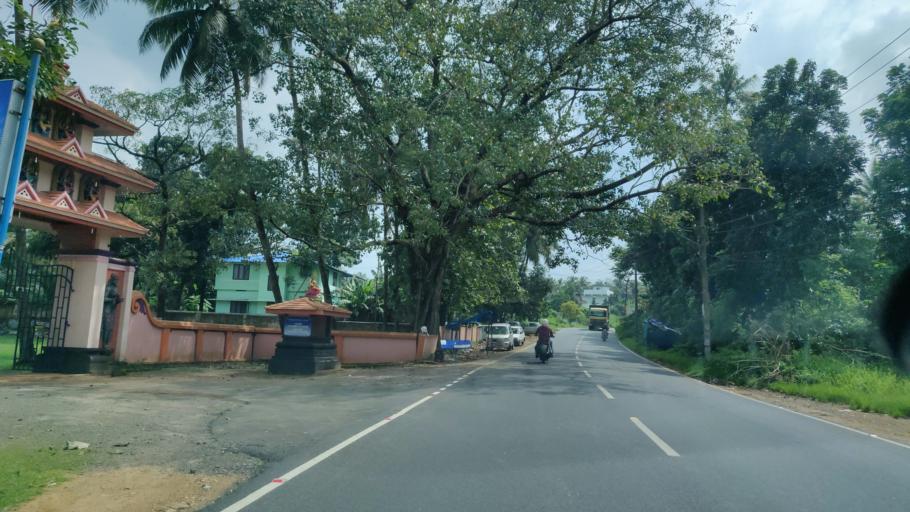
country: IN
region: Kerala
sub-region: Ernakulam
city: Angamali
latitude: 10.1688
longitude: 76.4217
